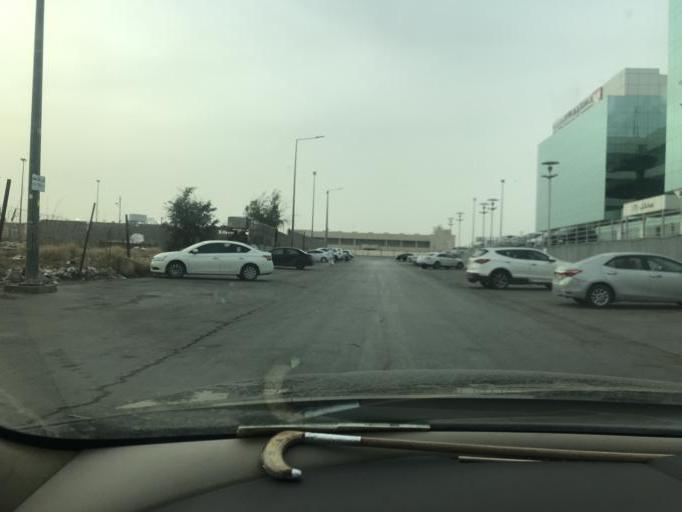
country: SA
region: Ar Riyad
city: Riyadh
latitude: 24.7206
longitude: 46.7745
